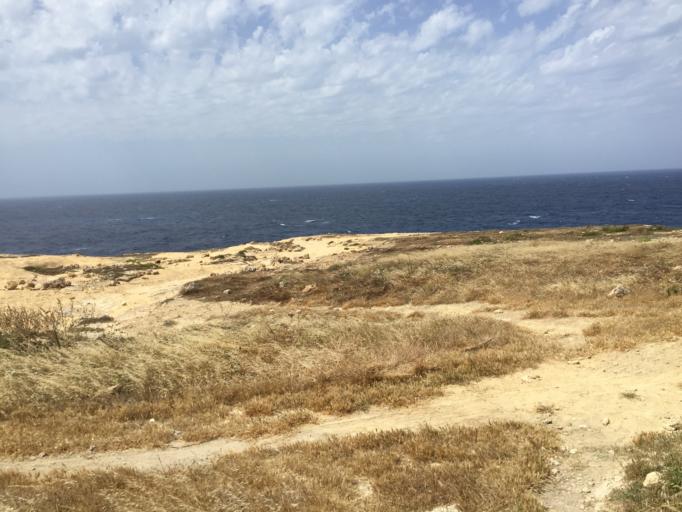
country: MT
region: L-Gharb
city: Gharb
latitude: 36.0774
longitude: 14.2038
